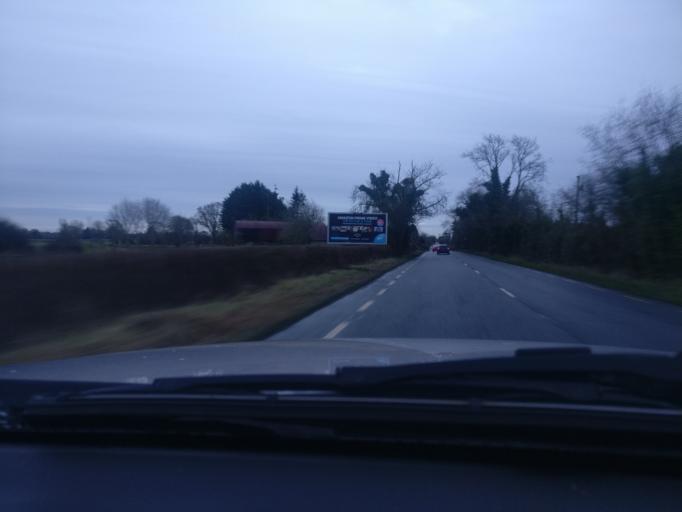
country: IE
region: Leinster
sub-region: An Mhi
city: Navan
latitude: 53.6898
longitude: -6.7754
